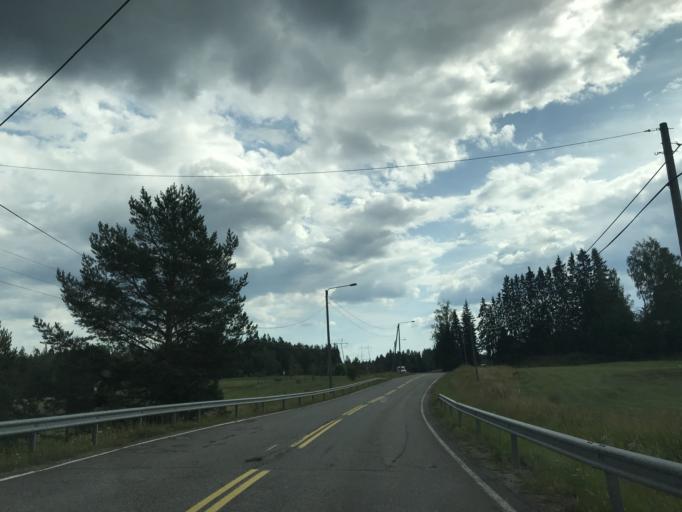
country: FI
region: Uusimaa
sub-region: Helsinki
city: Vihti
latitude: 60.3804
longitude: 24.3560
